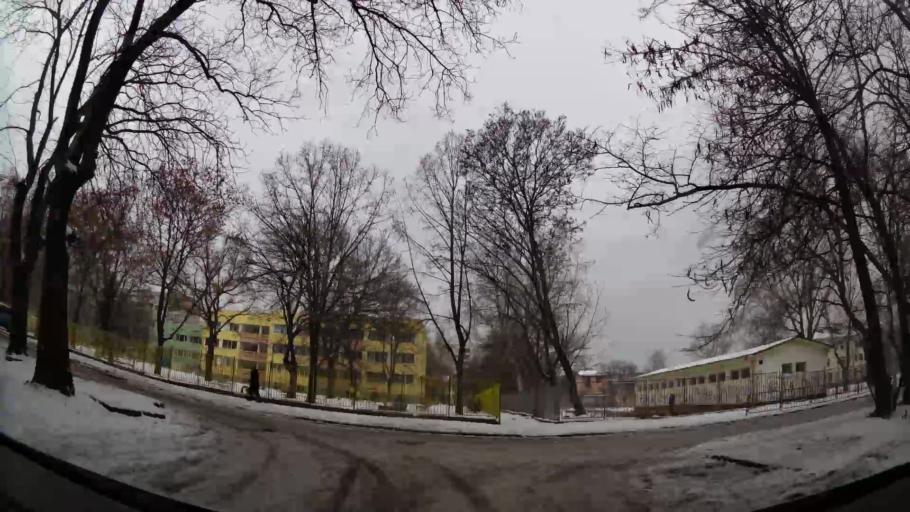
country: BG
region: Sofia-Capital
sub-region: Stolichna Obshtina
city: Sofia
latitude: 42.7138
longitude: 23.3017
